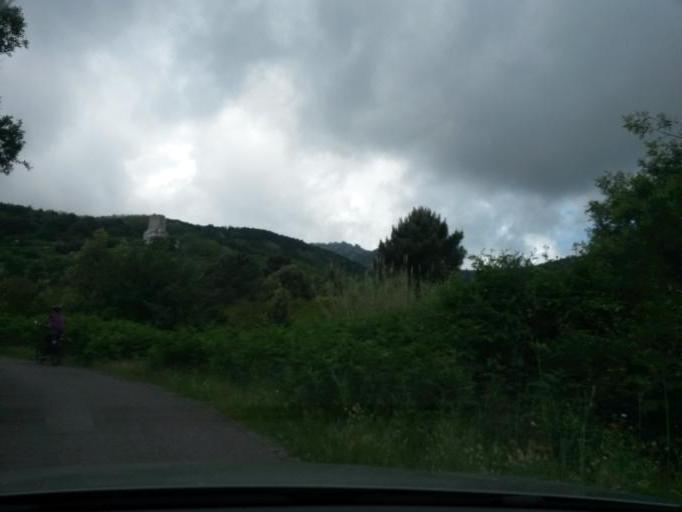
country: IT
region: Tuscany
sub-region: Provincia di Livorno
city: Campo nell'Elba
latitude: 42.7624
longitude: 10.2044
